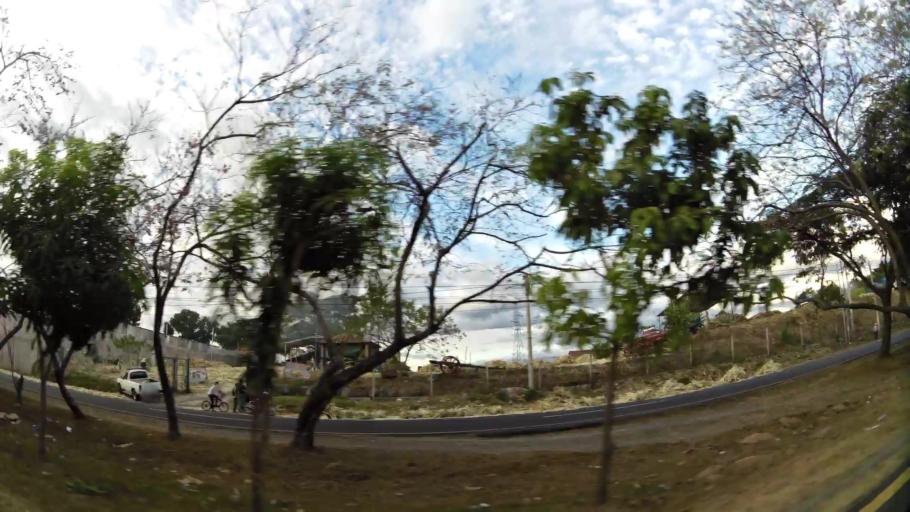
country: SV
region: San Vicente
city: San Vicente
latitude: 13.6700
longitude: -88.8344
